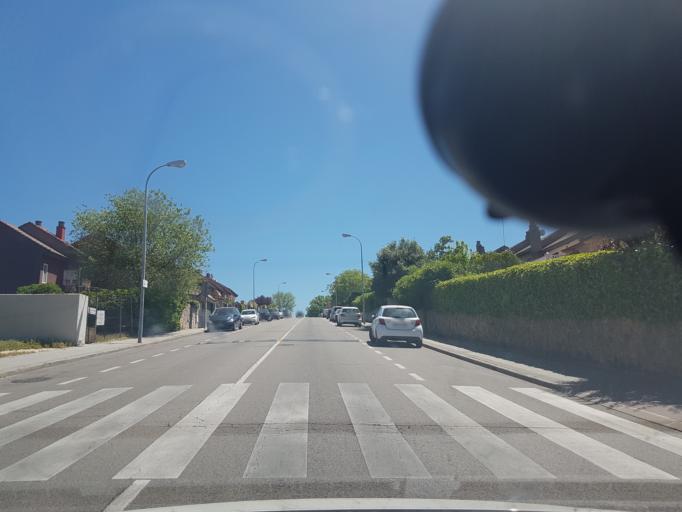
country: ES
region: Madrid
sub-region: Provincia de Madrid
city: Pozuelo de Alarcon
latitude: 40.4402
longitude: -3.8046
